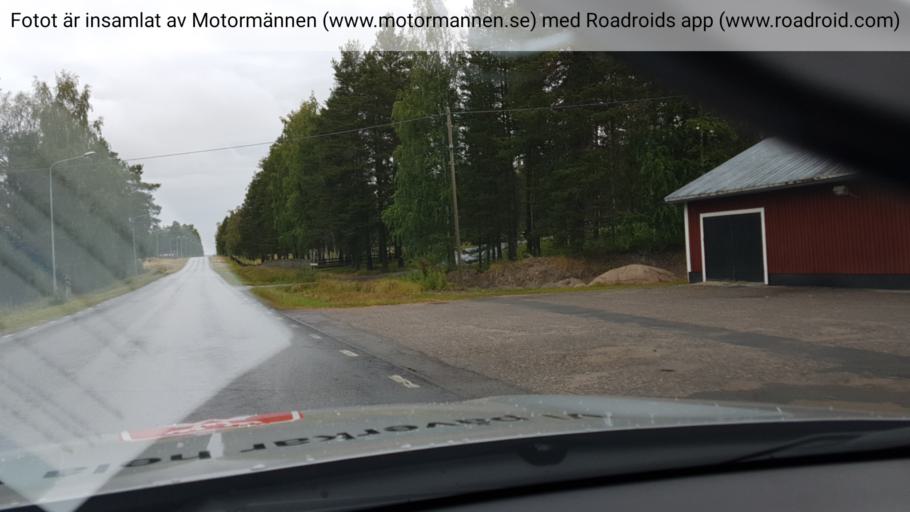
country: SE
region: Norrbotten
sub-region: Alvsbyns Kommun
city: AElvsbyn
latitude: 66.0898
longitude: 20.9474
